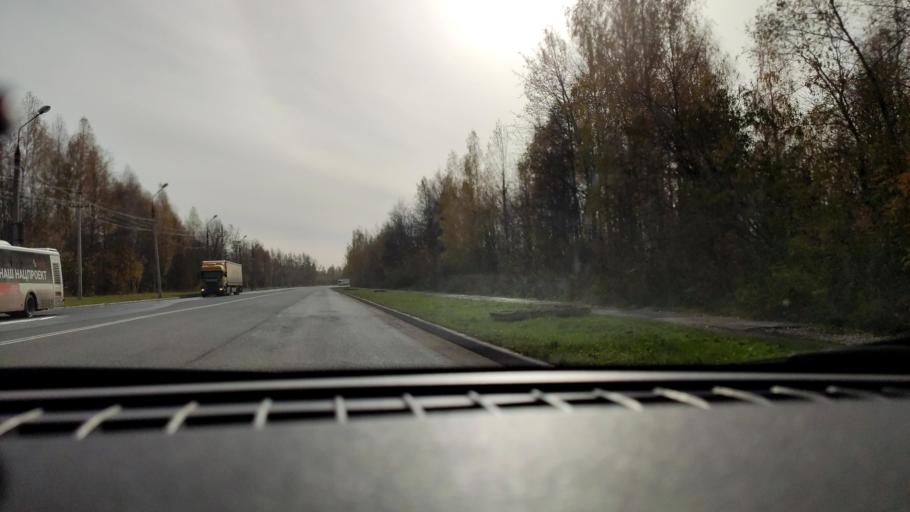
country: RU
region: Perm
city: Polazna
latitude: 58.1325
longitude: 56.4037
